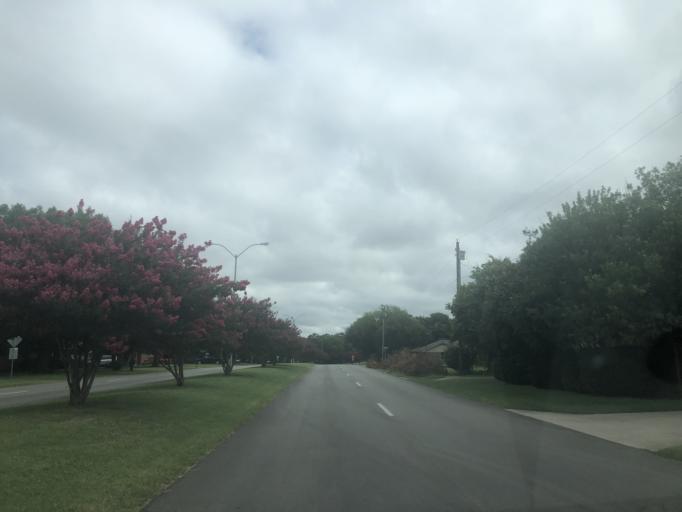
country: US
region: Texas
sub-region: Dallas County
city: Duncanville
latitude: 32.6628
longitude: -96.9170
